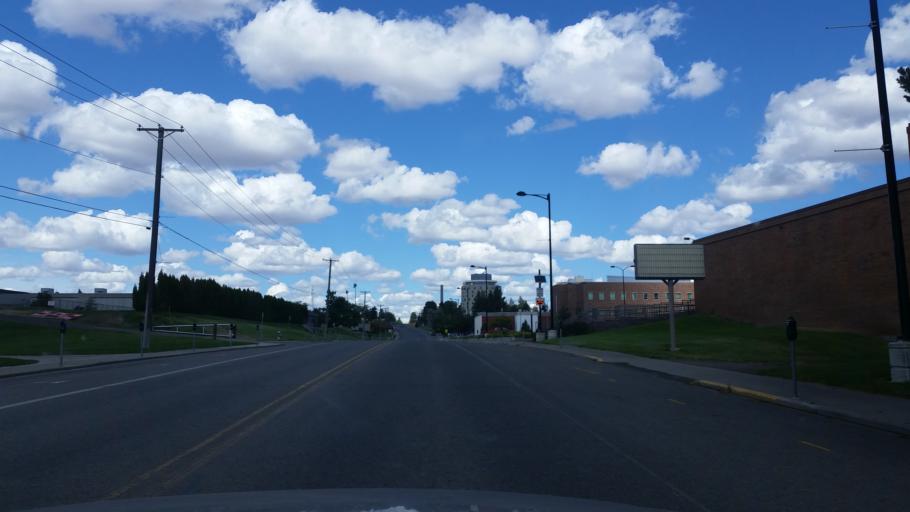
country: US
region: Washington
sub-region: Spokane County
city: Cheney
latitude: 47.4877
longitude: -117.5863
